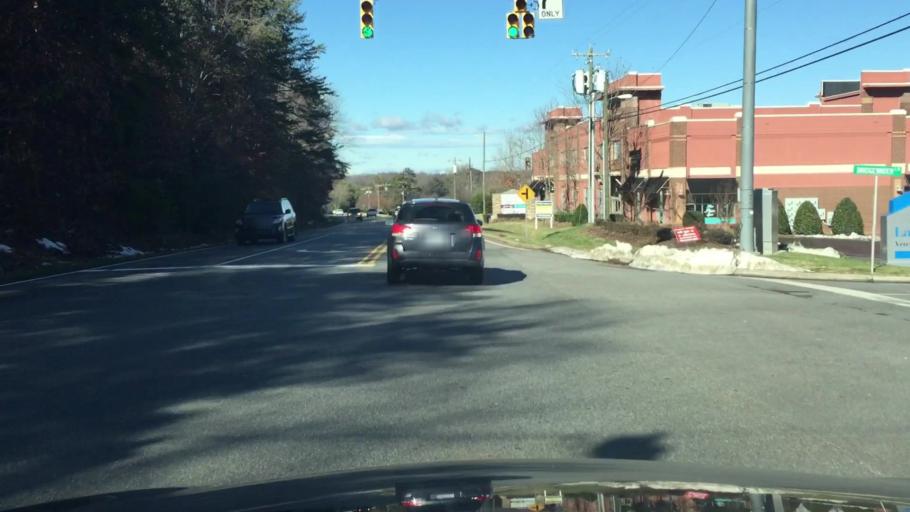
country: US
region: North Carolina
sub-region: Iredell County
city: Mooresville
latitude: 35.5572
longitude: -80.8623
